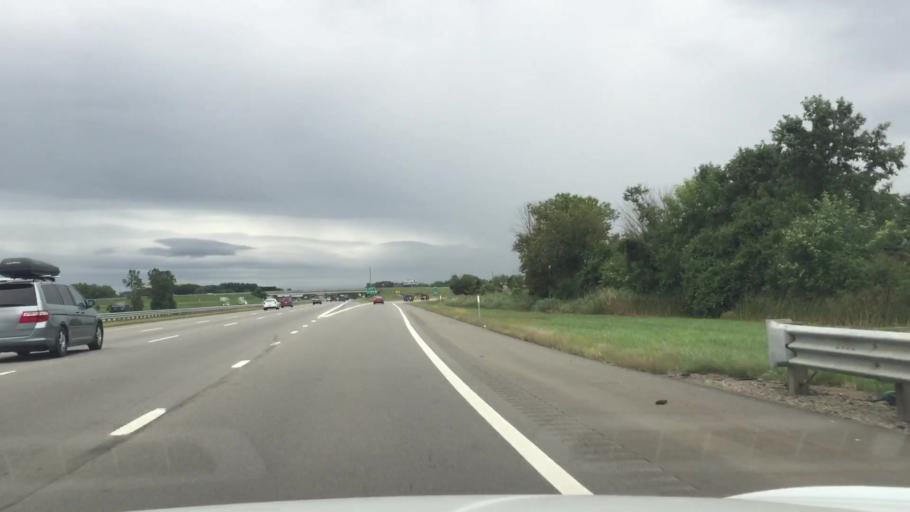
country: US
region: Michigan
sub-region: Macomb County
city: Mount Clemens
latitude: 42.6363
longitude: -82.8469
